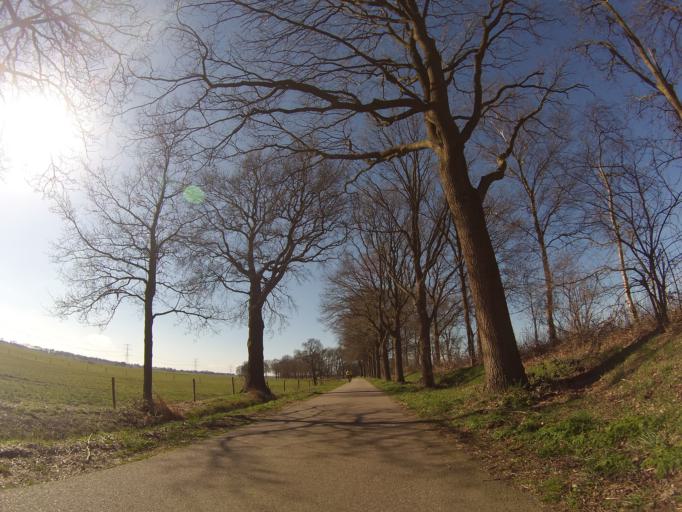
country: NL
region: Drenthe
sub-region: Gemeente Coevorden
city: Sleen
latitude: 52.7522
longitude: 6.8339
